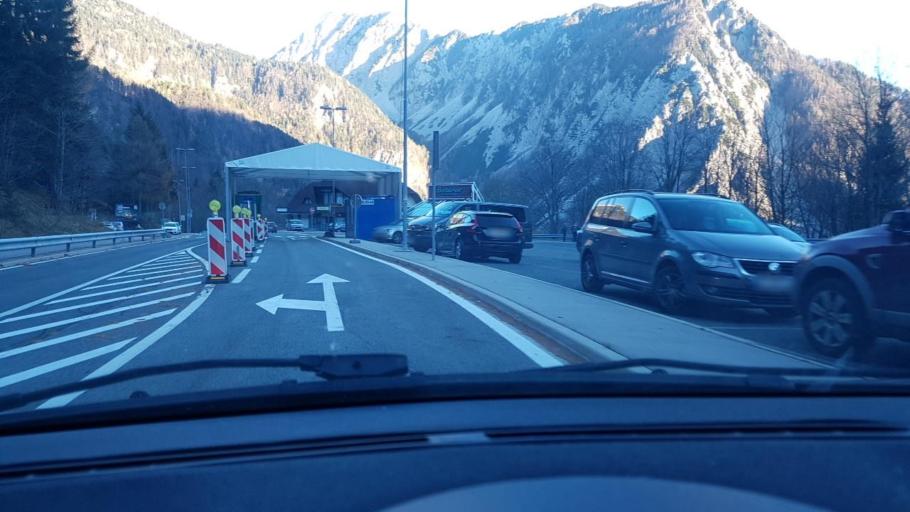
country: SI
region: Trzic
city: Bistrica pri Trzicu
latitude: 46.4328
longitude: 14.2604
